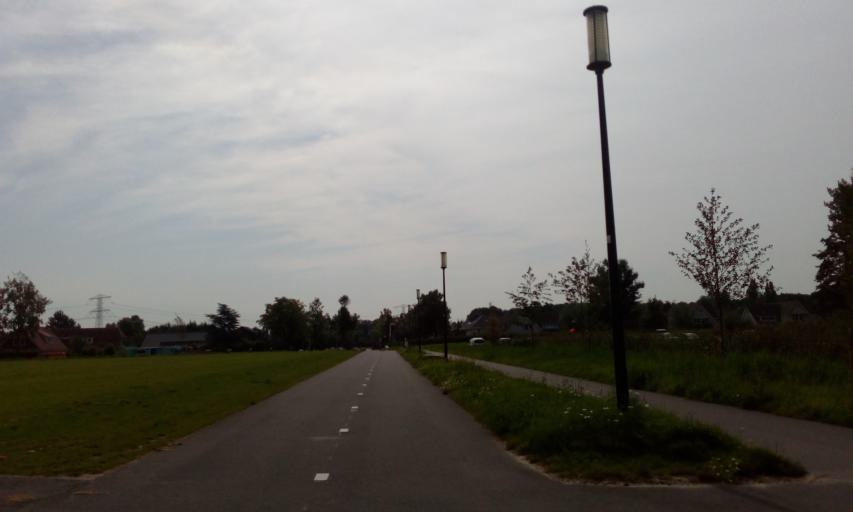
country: NL
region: South Holland
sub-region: Gemeente Capelle aan den IJssel
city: Capelle aan den IJssel
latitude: 51.9768
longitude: 4.5769
